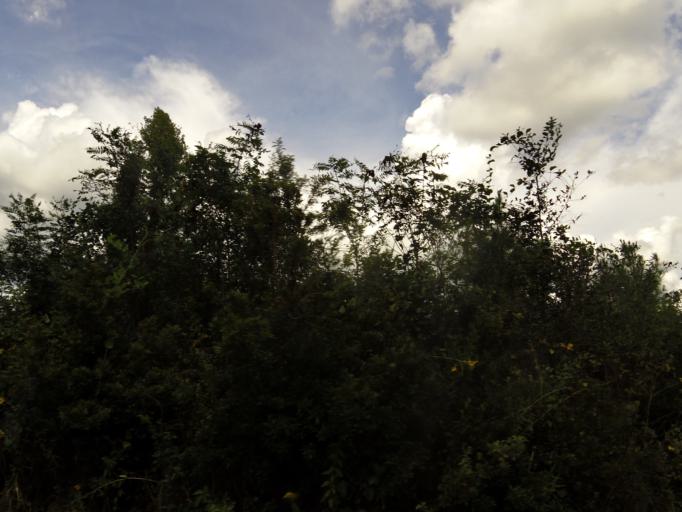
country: US
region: Georgia
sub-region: Brantley County
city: Nahunta
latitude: 31.0920
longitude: -82.0249
